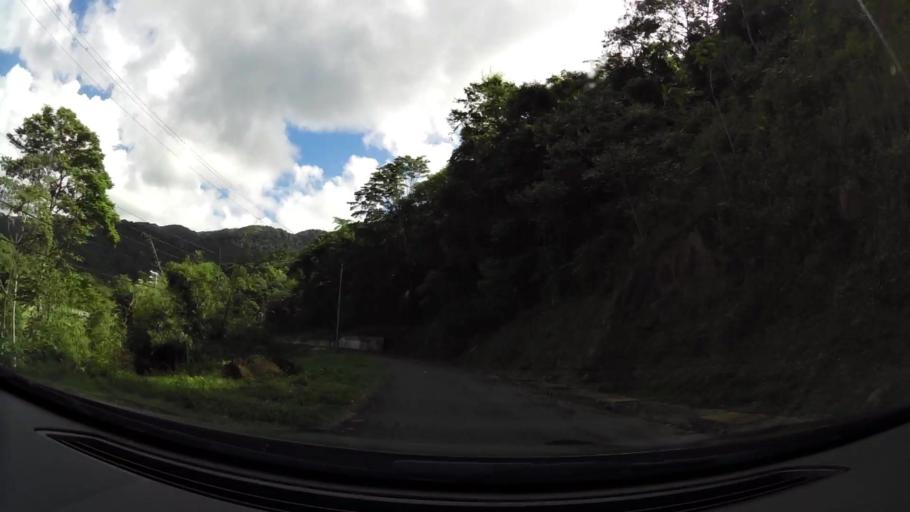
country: TT
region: Eastern Tobago
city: Roxborough
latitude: 11.3013
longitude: -60.6296
